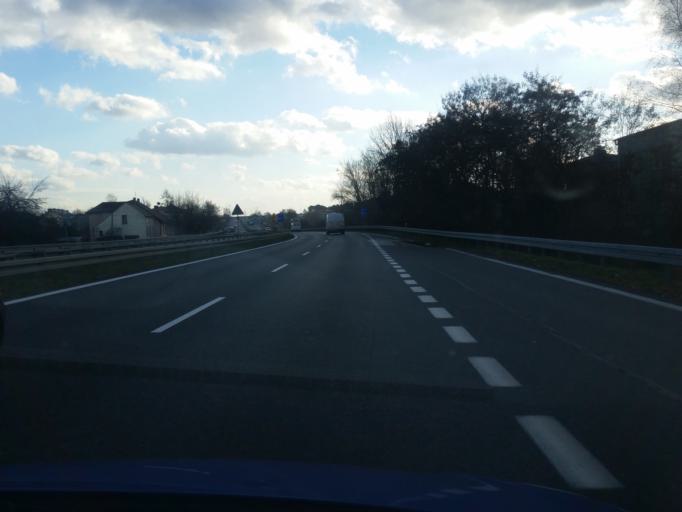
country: PL
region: Silesian Voivodeship
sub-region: Powiat bedzinski
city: Siewierz
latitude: 50.4738
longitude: 19.2283
